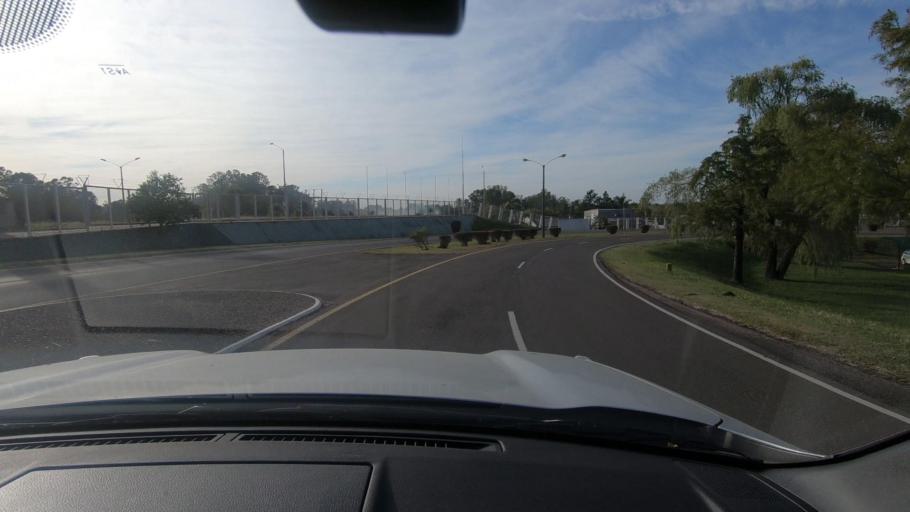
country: AR
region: Entre Rios
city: Colon
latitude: -32.2463
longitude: -58.1476
